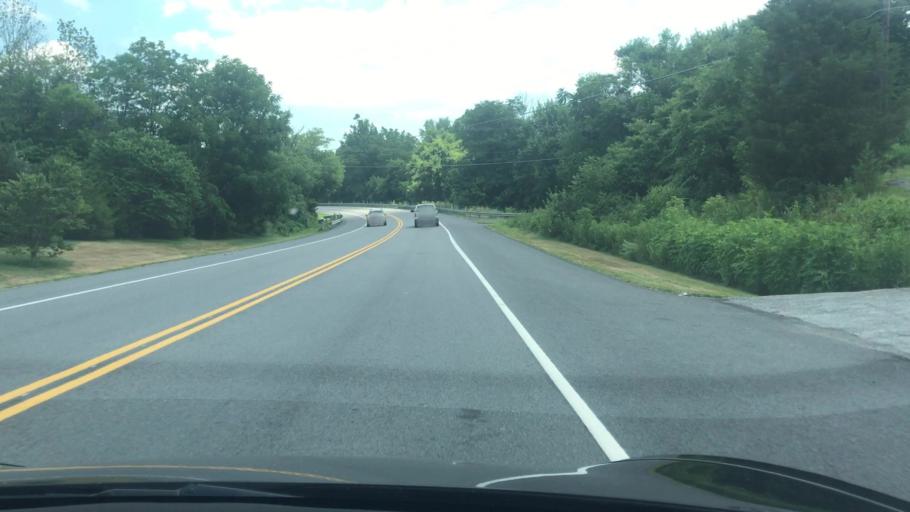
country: US
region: Pennsylvania
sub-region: York County
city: Valley Green
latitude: 40.1303
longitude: -76.8336
